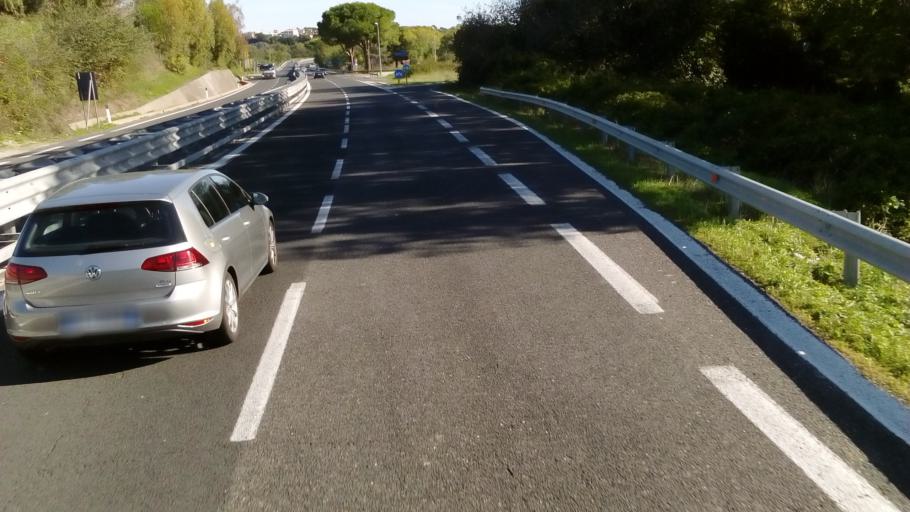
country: IT
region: Latium
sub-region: Provincia di Viterbo
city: Montalto di Castro
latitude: 42.3573
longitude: 11.5890
